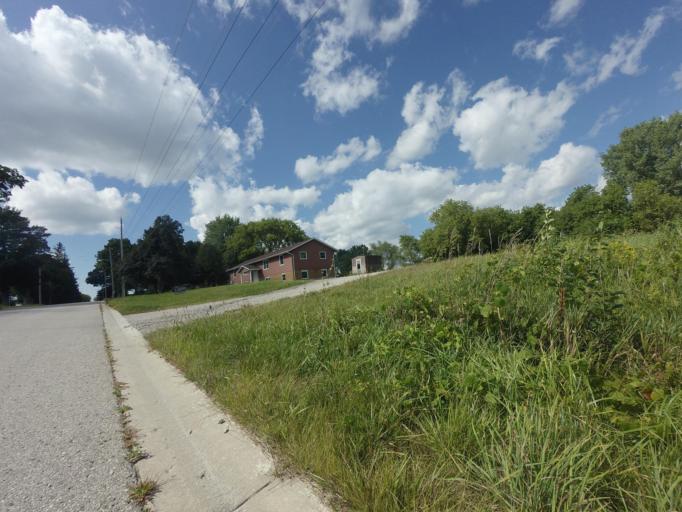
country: CA
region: Ontario
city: Huron East
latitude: 43.7312
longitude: -81.4174
